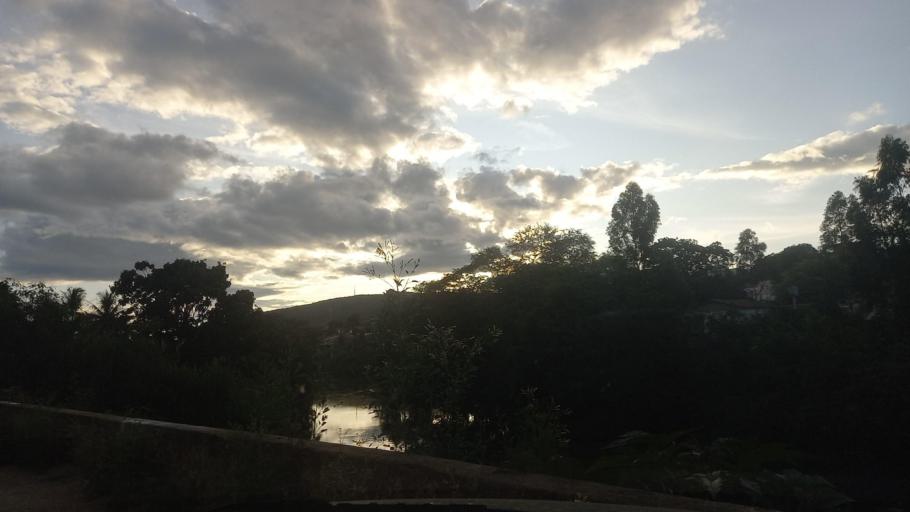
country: BR
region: Pernambuco
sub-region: Bezerros
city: Bezerros
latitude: -8.2346
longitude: -35.7539
